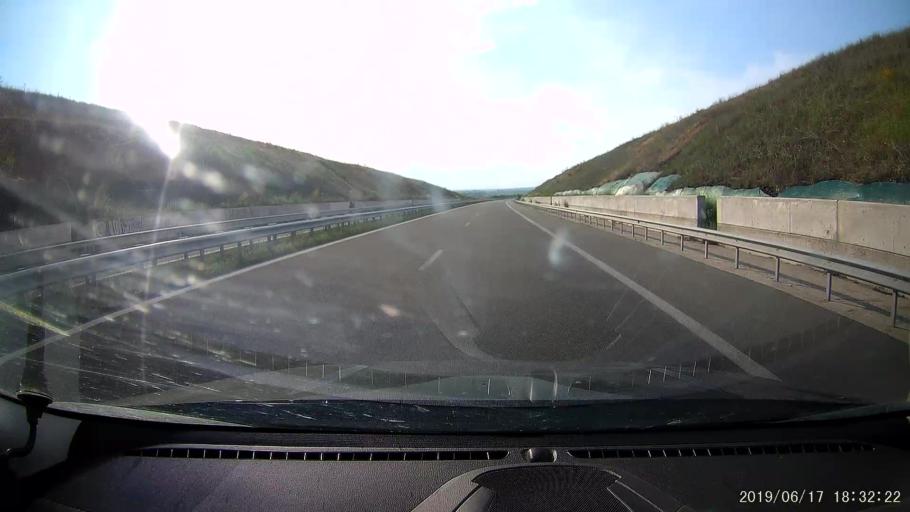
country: BG
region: Khaskovo
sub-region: Obshtina Dimitrovgrad
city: Dimitrovgrad
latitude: 42.0586
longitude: 25.4805
